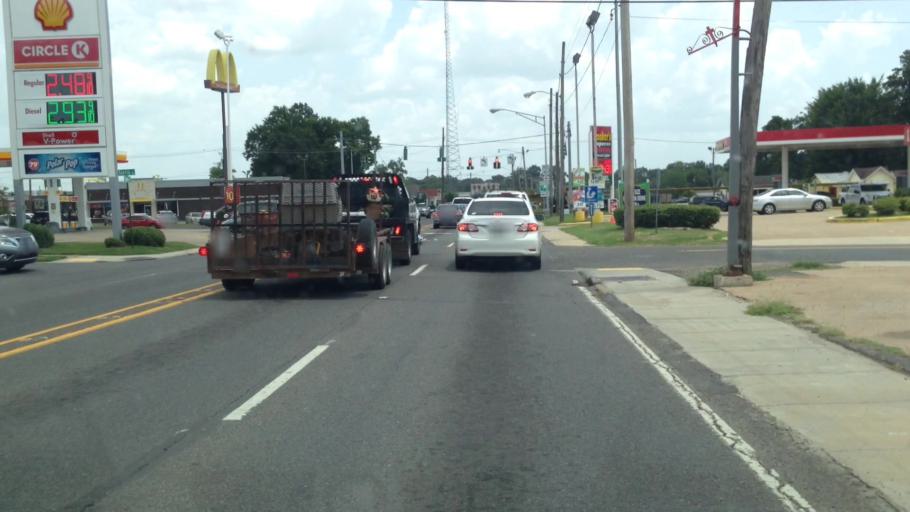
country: US
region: Louisiana
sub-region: Ouachita Parish
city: Monroe
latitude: 32.5045
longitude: -92.1290
